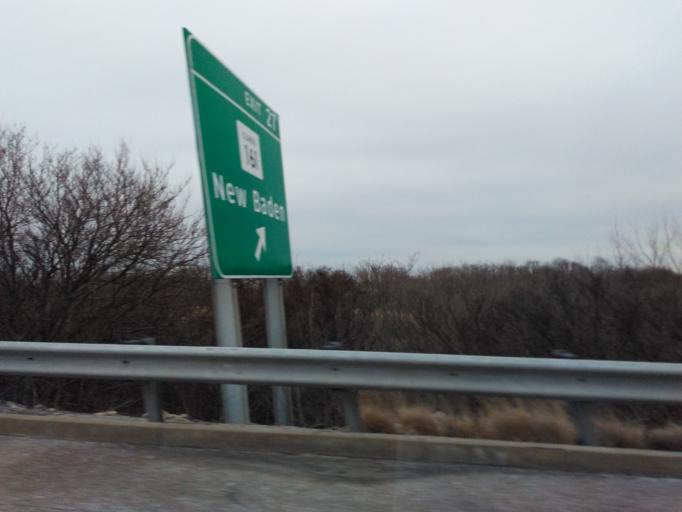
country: US
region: Illinois
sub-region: Clinton County
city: New Baden
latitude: 38.5310
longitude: -89.7251
